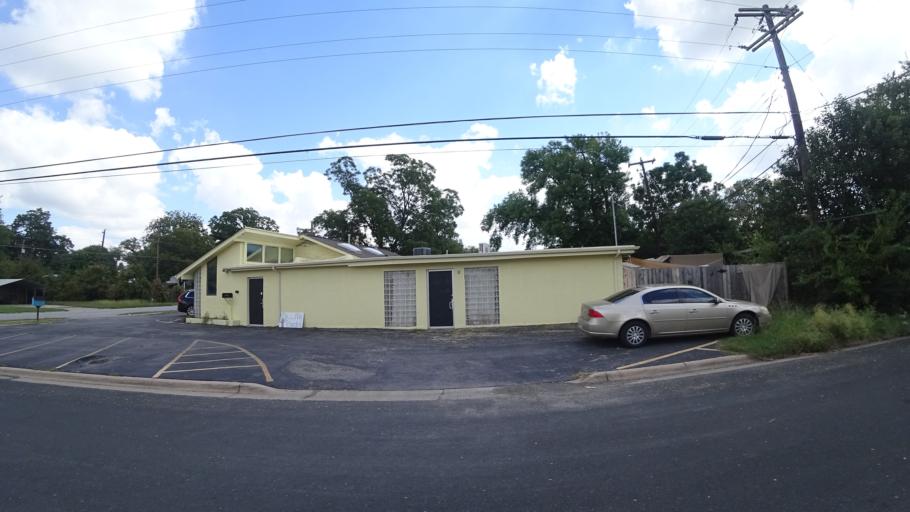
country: US
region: Texas
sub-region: Williamson County
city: Jollyville
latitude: 30.3623
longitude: -97.7282
